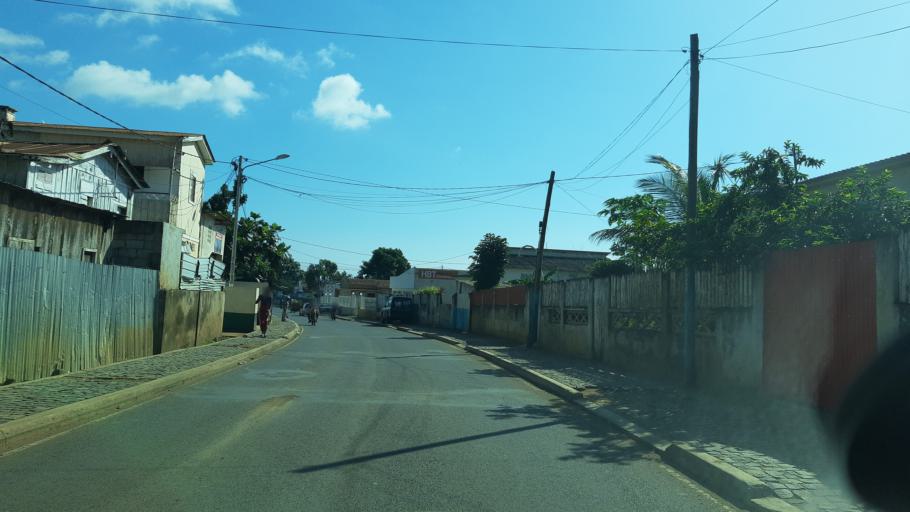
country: ST
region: Sao Tome Island
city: Sao Tome
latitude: 0.3301
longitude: 6.7302
